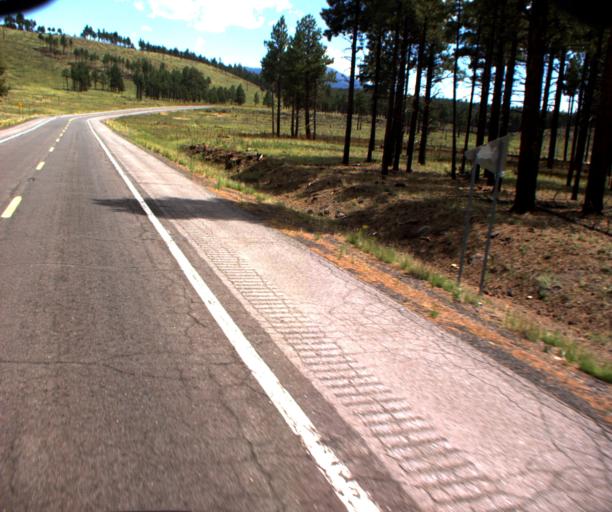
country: US
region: Arizona
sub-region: Coconino County
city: Parks
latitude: 35.4461
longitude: -111.7648
